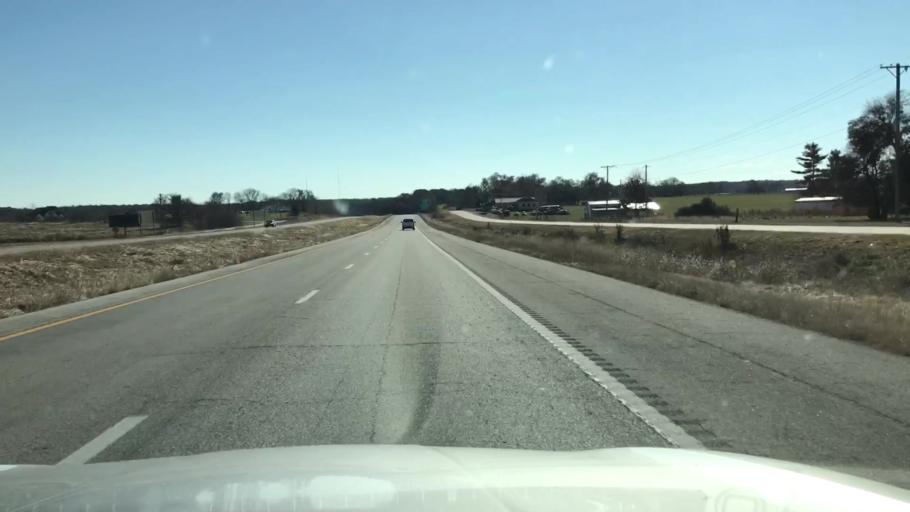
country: US
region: Missouri
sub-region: Jasper County
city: Carthage
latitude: 37.1206
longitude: -94.3112
